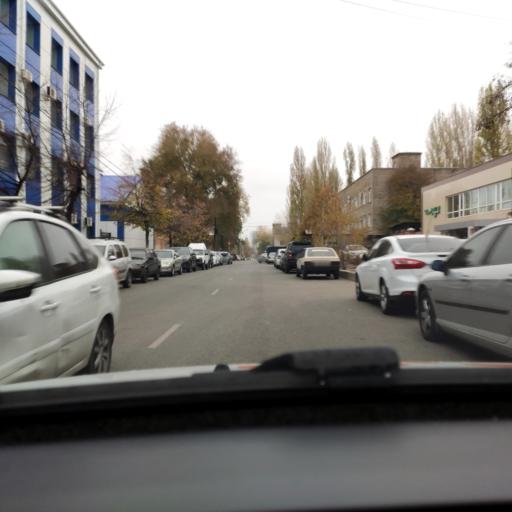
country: RU
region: Voronezj
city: Voronezh
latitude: 51.6602
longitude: 39.1563
